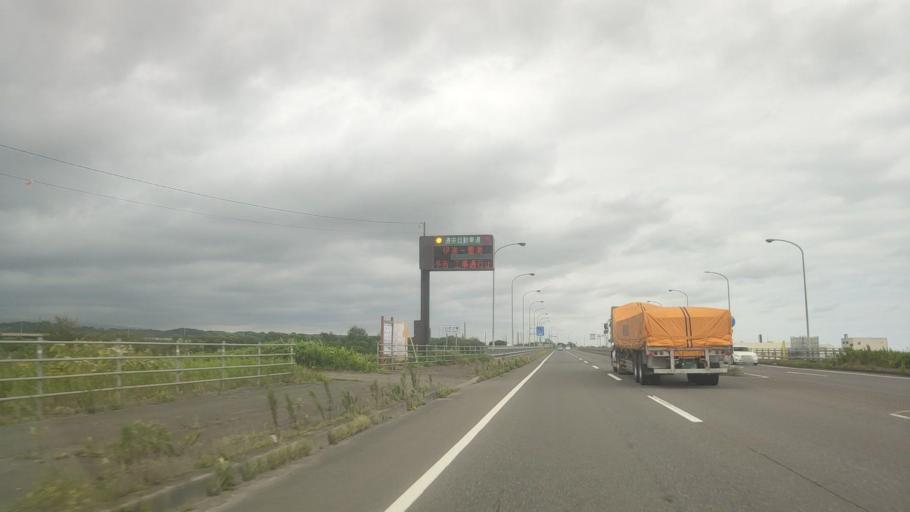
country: JP
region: Hokkaido
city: Shiraoi
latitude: 42.5418
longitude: 141.3442
